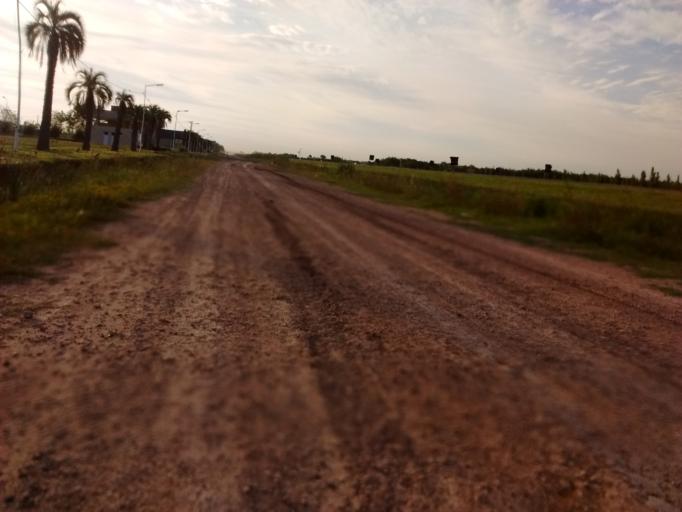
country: AR
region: Santa Fe
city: Roldan
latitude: -32.9307
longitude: -60.8742
